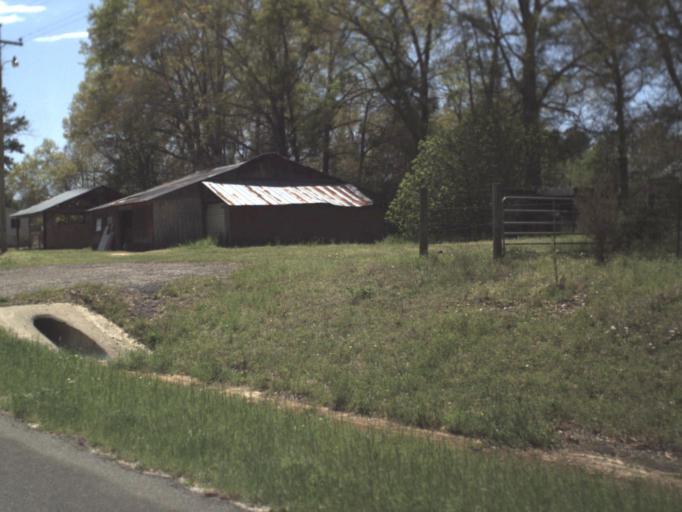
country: US
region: Florida
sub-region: Walton County
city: DeFuniak Springs
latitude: 30.7689
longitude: -85.9589
